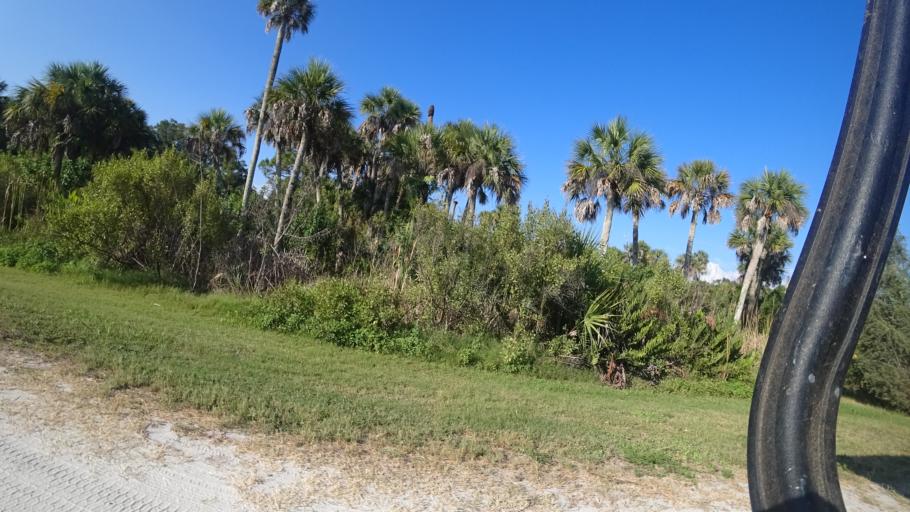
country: US
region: Florida
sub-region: Manatee County
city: Ellenton
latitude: 27.4981
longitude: -82.4885
